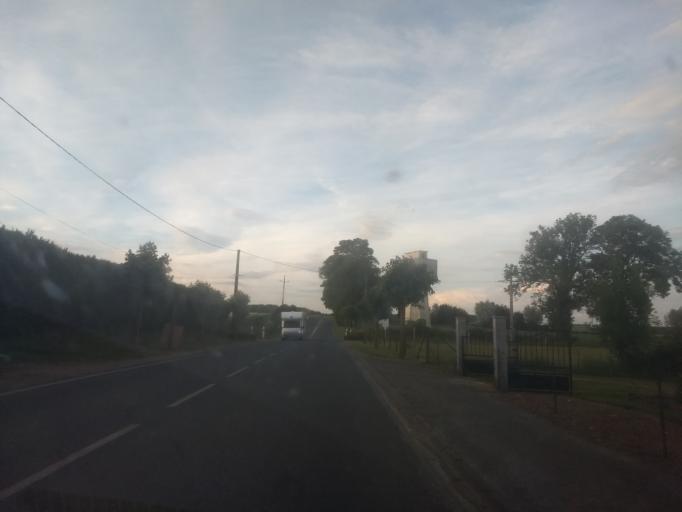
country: FR
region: Nord-Pas-de-Calais
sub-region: Departement du Pas-de-Calais
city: Bucquoy
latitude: 50.1214
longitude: 2.6929
